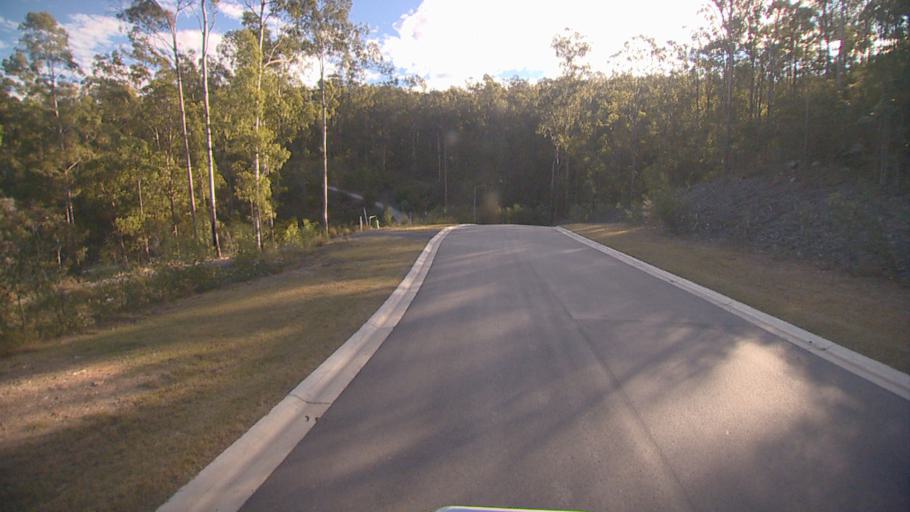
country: AU
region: Queensland
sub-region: Logan
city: Cedar Vale
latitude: -27.9275
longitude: 153.0519
